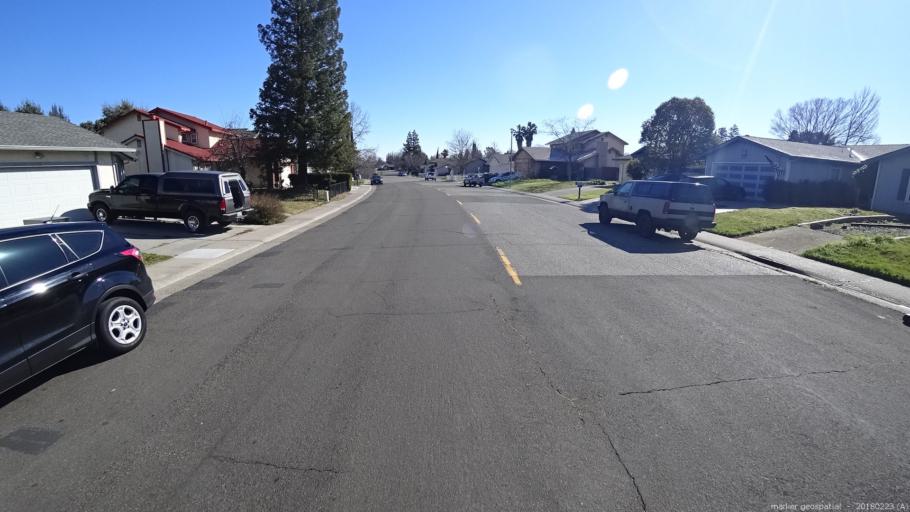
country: US
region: California
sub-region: Sacramento County
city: North Highlands
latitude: 38.7085
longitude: -121.3779
